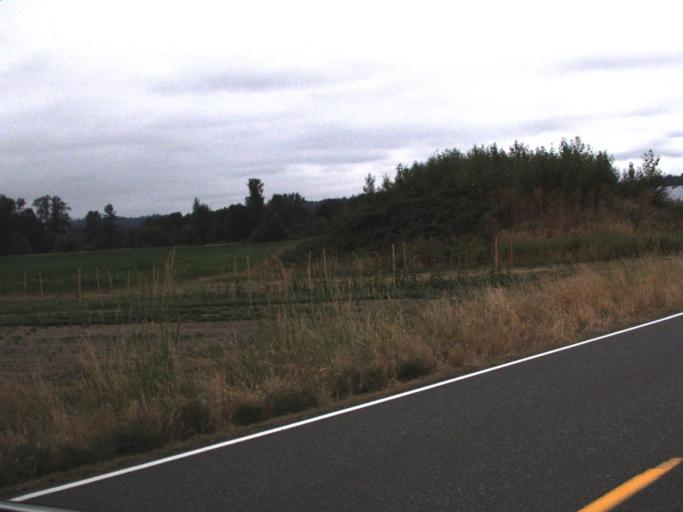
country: US
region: Washington
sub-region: King County
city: Carnation
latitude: 47.6594
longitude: -121.9102
